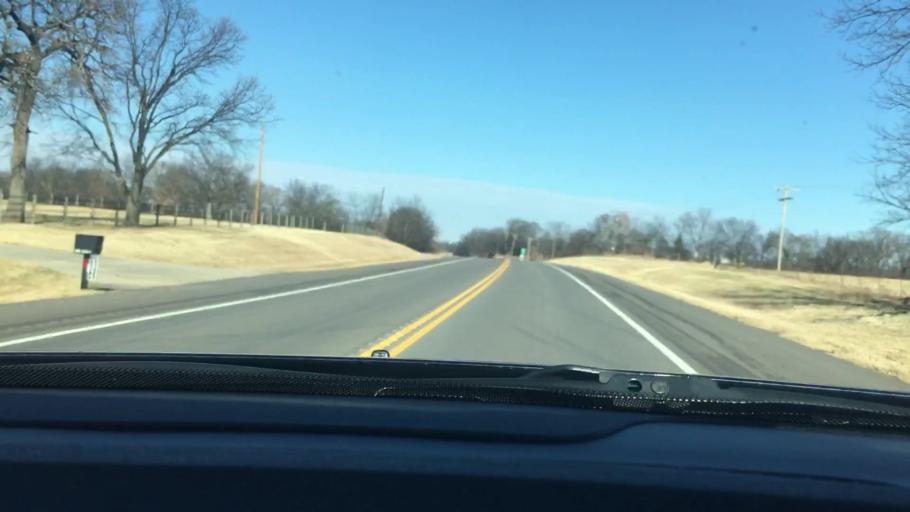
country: US
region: Oklahoma
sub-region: Murray County
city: Davis
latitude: 34.5178
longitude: -97.1207
